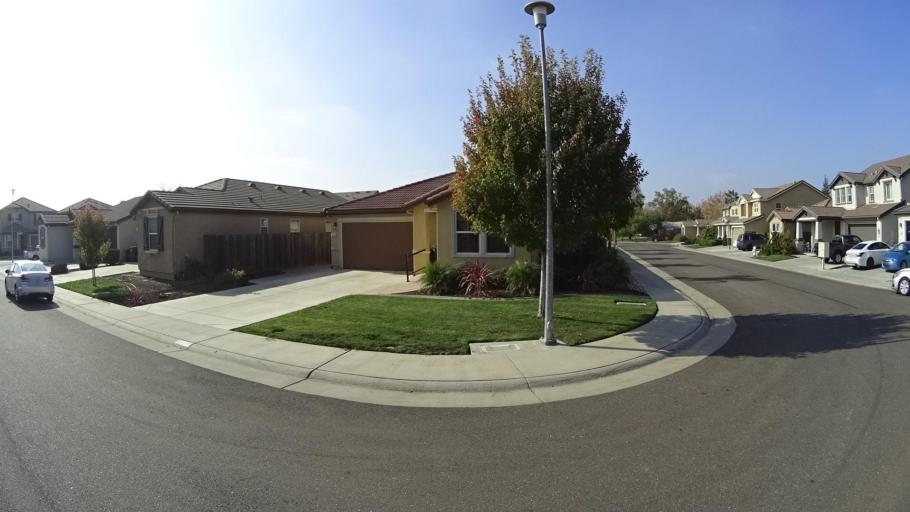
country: US
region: California
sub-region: Sacramento County
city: Vineyard
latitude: 38.4519
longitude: -121.3630
